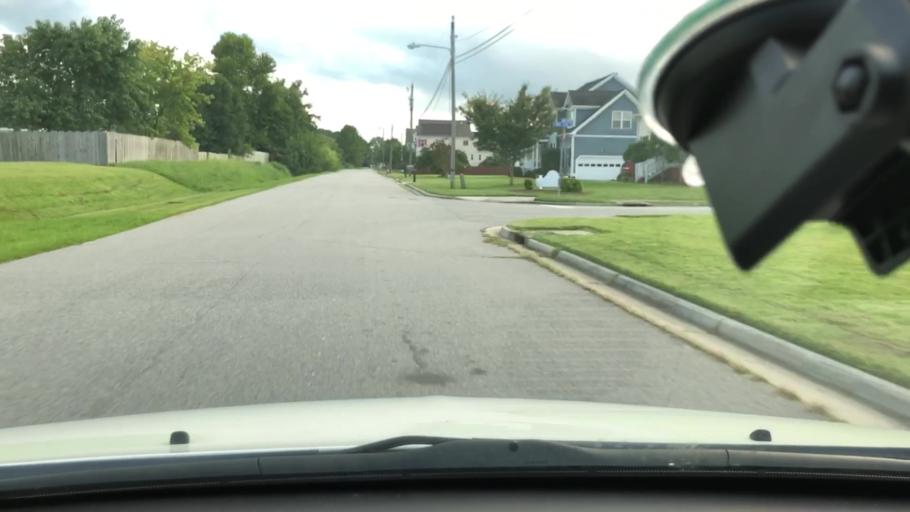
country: US
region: Virginia
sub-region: City of Chesapeake
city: Chesapeake
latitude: 36.7225
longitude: -76.2729
